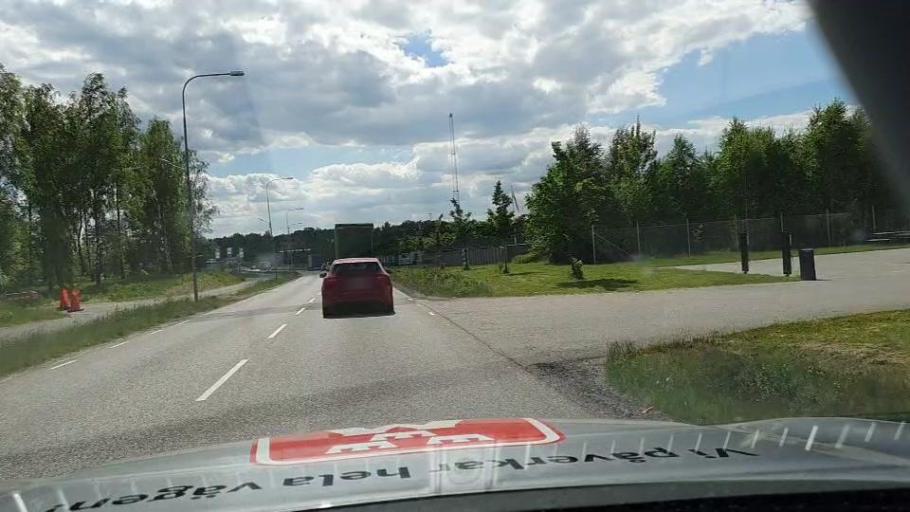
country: SE
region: Kronoberg
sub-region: Ljungby Kommun
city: Ljungby
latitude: 56.8479
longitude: 13.9242
